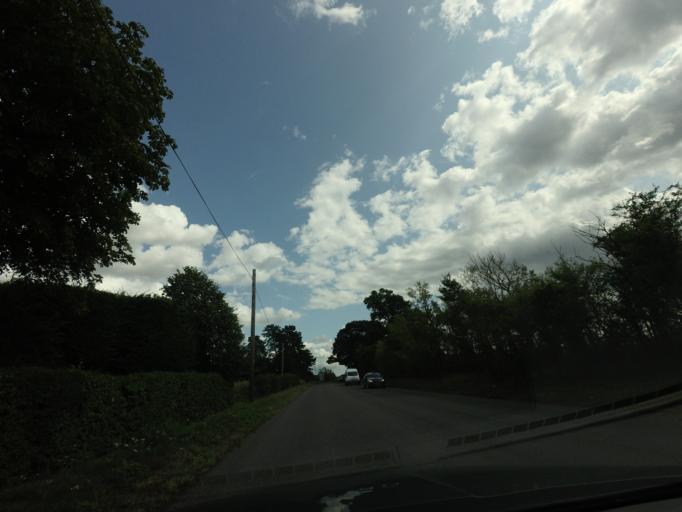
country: GB
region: England
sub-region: Kent
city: Harrietsham
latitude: 51.2638
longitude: 0.6063
